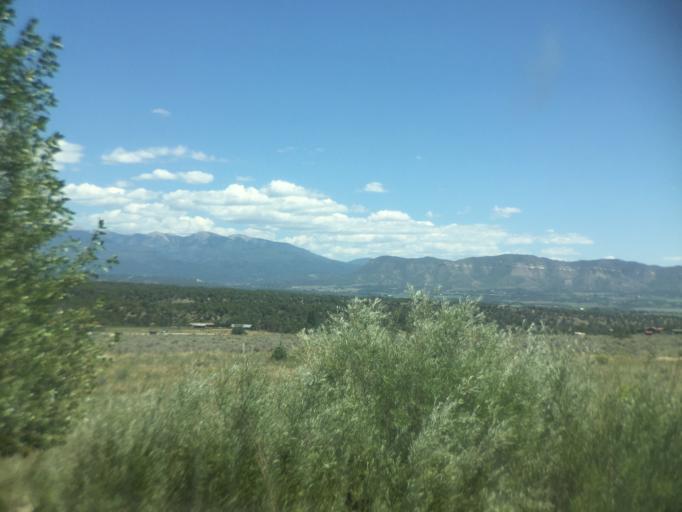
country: US
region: Colorado
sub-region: Montezuma County
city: Mancos
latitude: 37.3367
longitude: -108.4076
